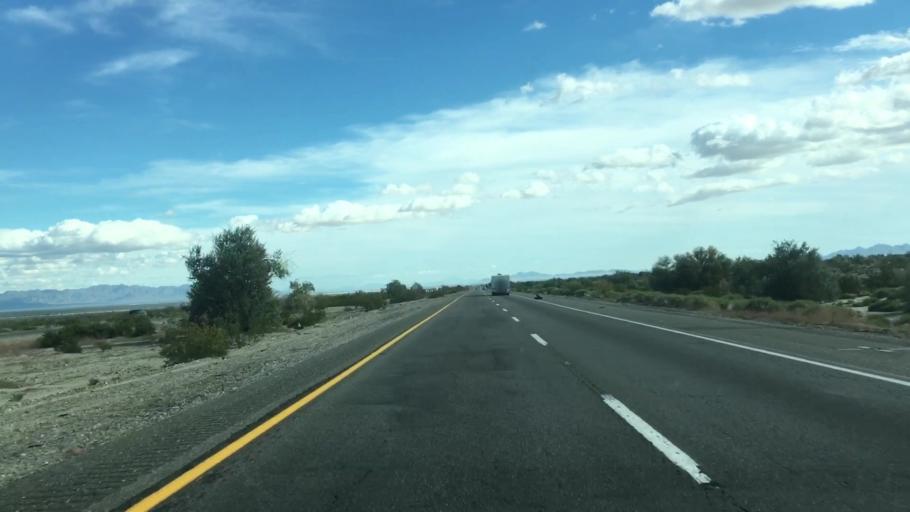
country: US
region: California
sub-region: Riverside County
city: Mesa Verde
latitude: 33.6744
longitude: -115.2171
